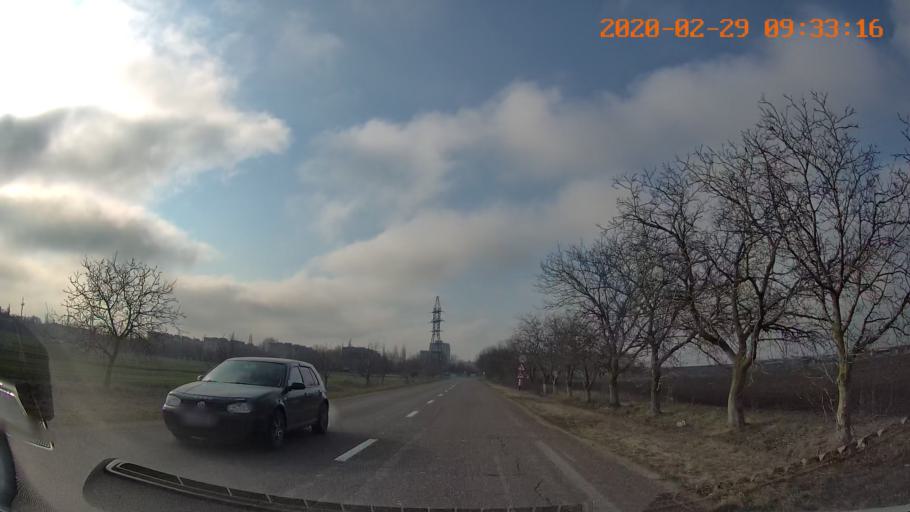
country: MD
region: Telenesti
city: Dnestrovsc
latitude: 46.6296
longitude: 29.9022
